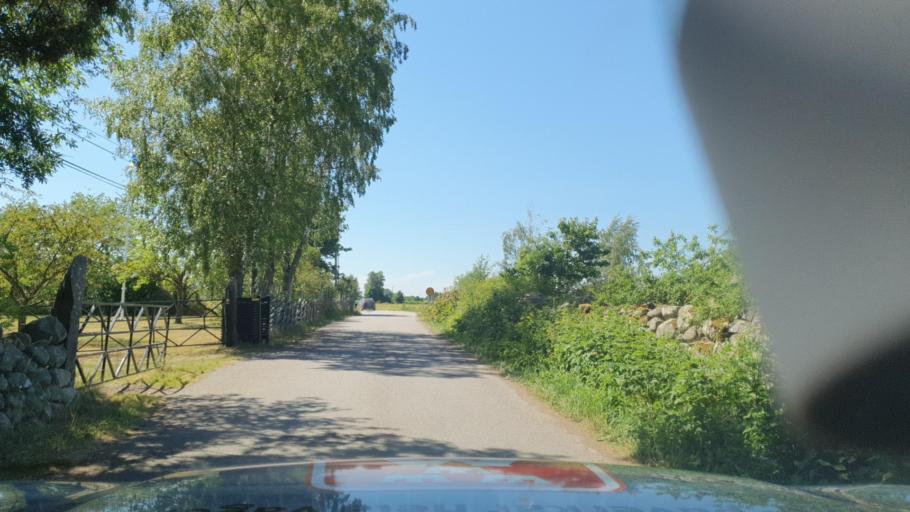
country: SE
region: Kalmar
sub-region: Torsas Kommun
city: Torsas
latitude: 56.3647
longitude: 16.0712
